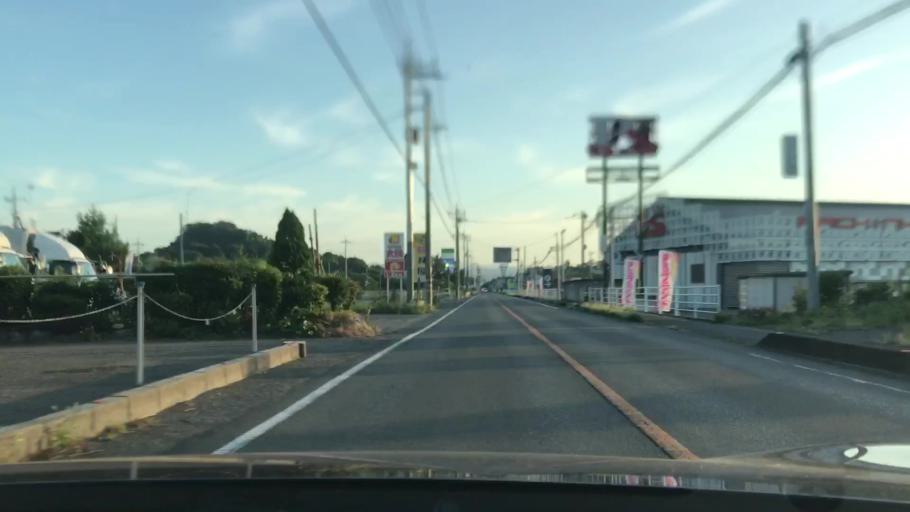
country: JP
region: Gunma
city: Ota
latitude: 36.3087
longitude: 139.3864
